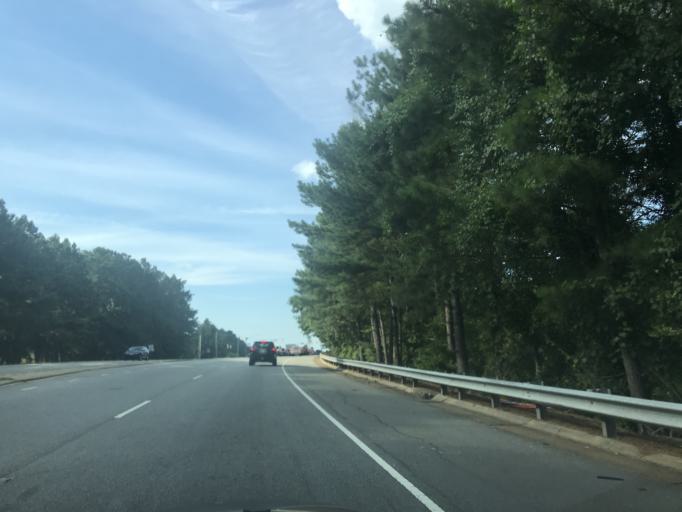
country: US
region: North Carolina
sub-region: Wake County
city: Raleigh
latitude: 35.7408
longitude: -78.6409
